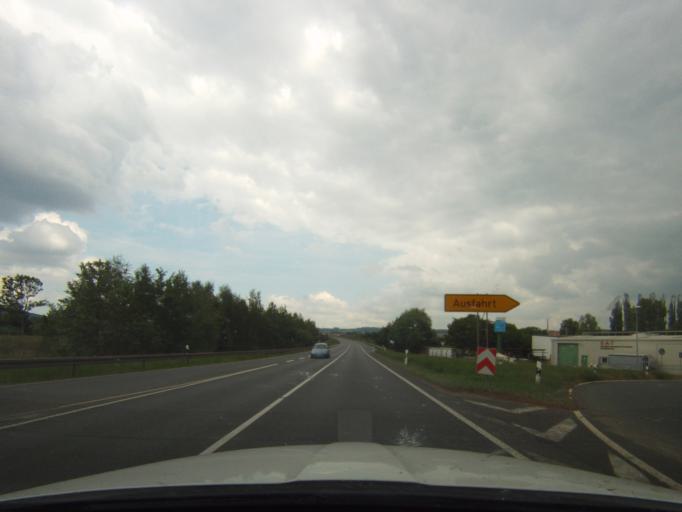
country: DE
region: Thuringia
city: Saalfeld
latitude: 50.6592
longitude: 11.3675
